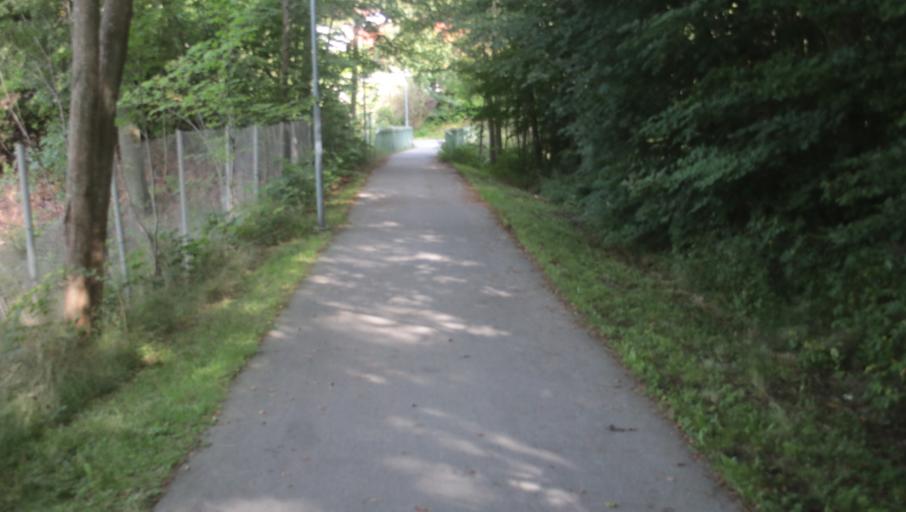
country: SE
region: Blekinge
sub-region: Karlshamns Kommun
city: Karlshamn
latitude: 56.1922
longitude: 14.8475
